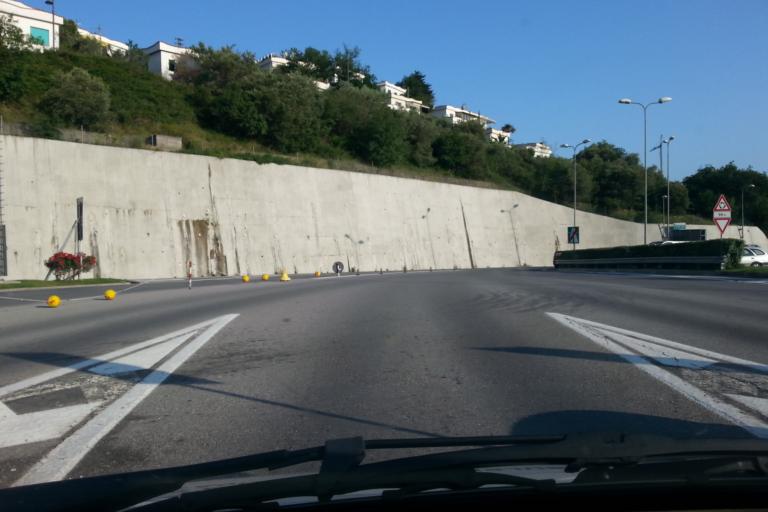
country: IT
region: Liguria
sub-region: Provincia di Savona
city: Pietra Ligure
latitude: 44.1550
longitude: 8.2710
